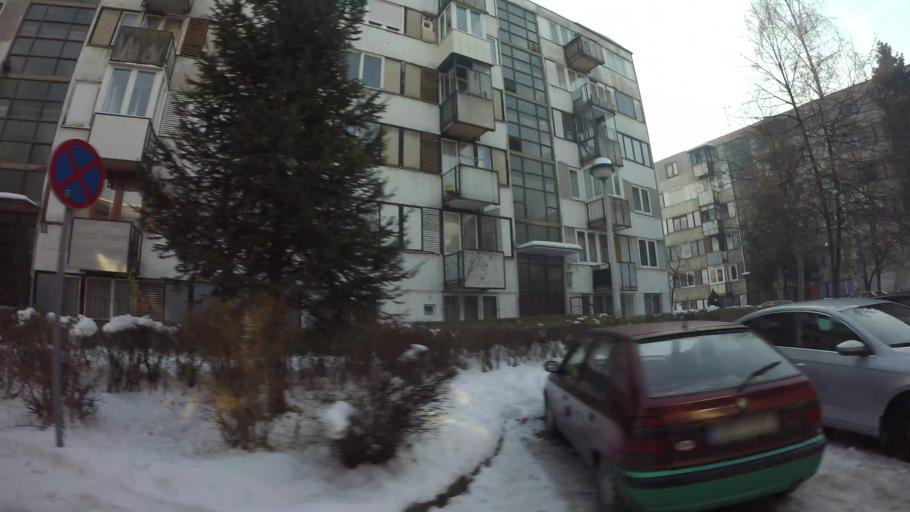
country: BA
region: Federation of Bosnia and Herzegovina
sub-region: Kanton Sarajevo
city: Sarajevo
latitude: 43.8460
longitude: 18.3687
